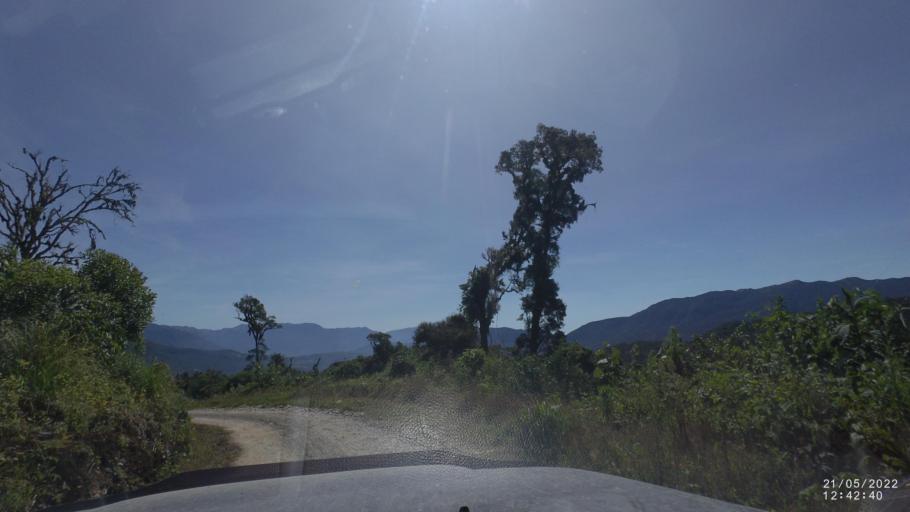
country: BO
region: Cochabamba
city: Colomi
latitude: -17.1915
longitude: -65.9302
